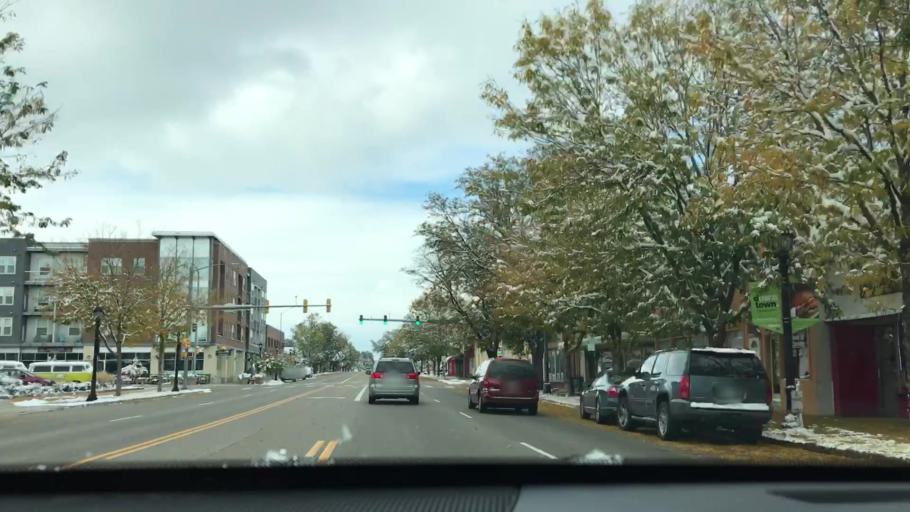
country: US
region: Colorado
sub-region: Boulder County
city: Longmont
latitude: 40.1699
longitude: -105.1025
